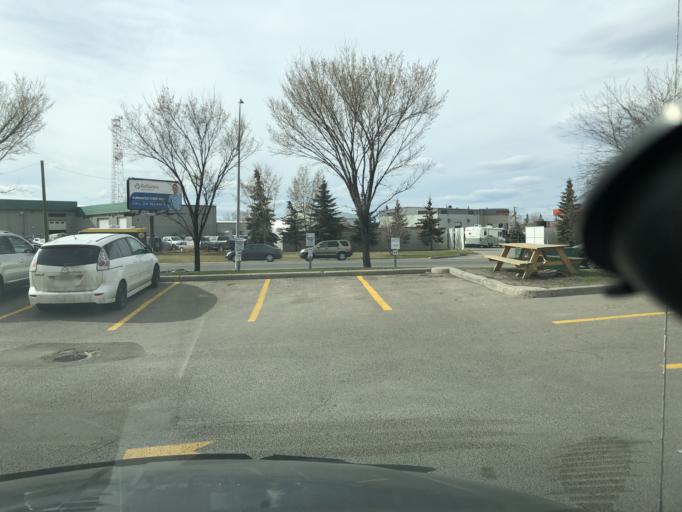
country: CA
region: Alberta
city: Calgary
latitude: 51.0690
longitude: -114.0046
